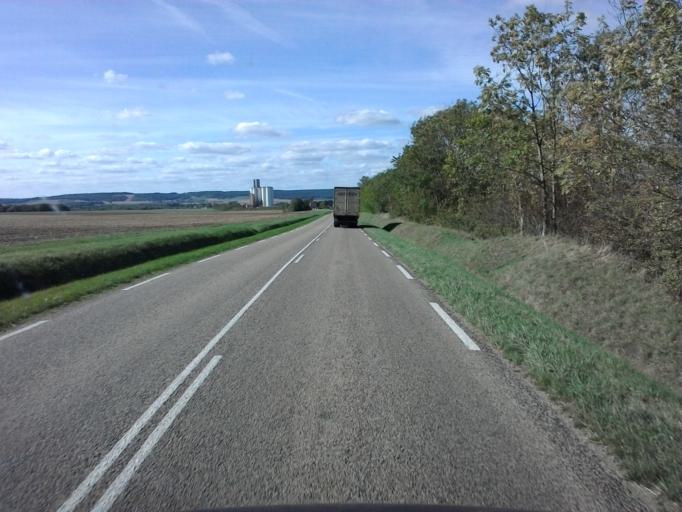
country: FR
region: Bourgogne
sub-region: Departement de la Cote-d'Or
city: Chatillon-sur-Seine
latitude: 47.9057
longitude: 4.6908
